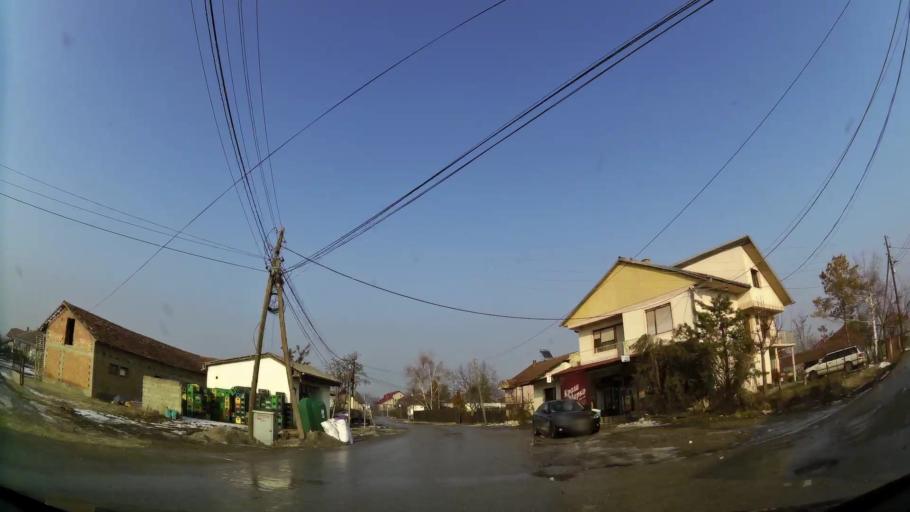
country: MK
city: Kadino
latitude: 41.9669
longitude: 21.5999
